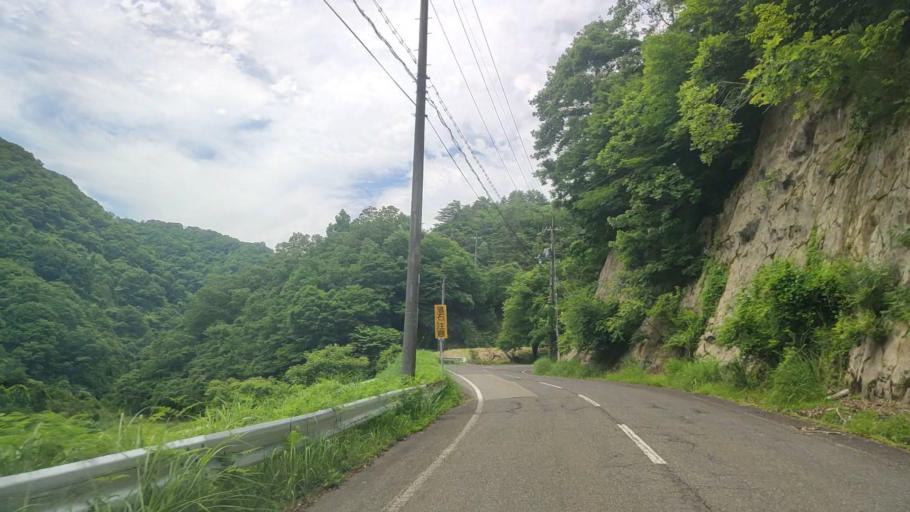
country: JP
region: Hyogo
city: Toyooka
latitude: 35.5216
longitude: 134.6958
